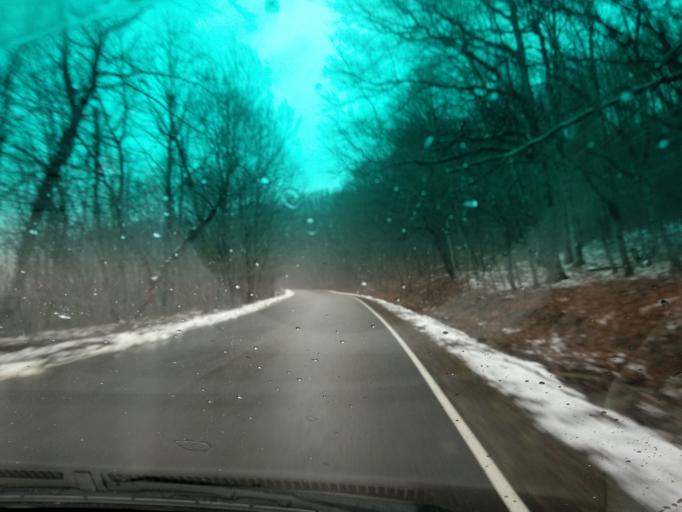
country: RU
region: Krasnodarskiy
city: Khadyzhensk
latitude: 44.2642
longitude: 39.3640
